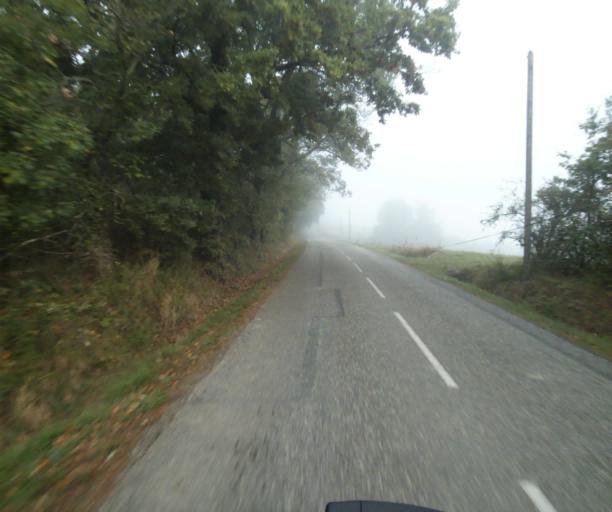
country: FR
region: Midi-Pyrenees
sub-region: Departement du Tarn-et-Garonne
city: Saint-Nauphary
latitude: 43.9414
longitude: 1.4147
